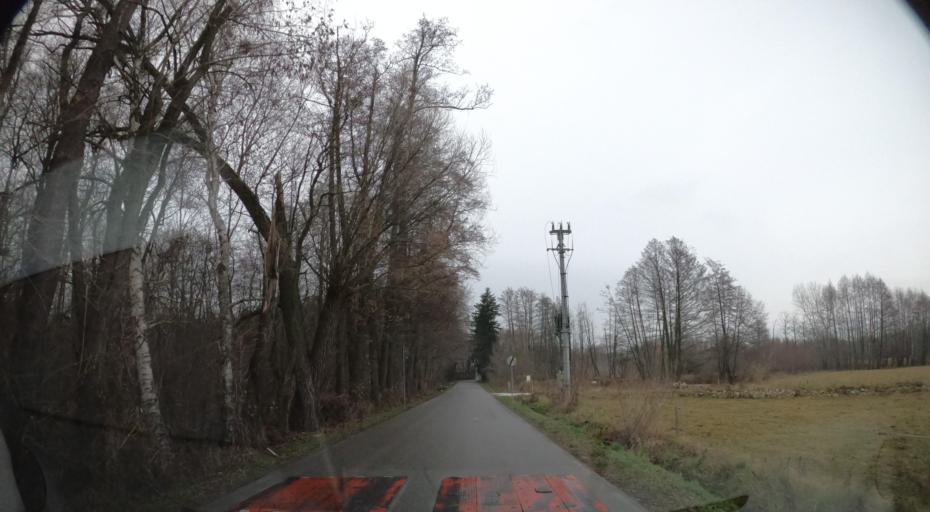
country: PL
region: Masovian Voivodeship
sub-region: Powiat radomski
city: Jastrzebia
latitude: 51.4231
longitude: 21.2271
